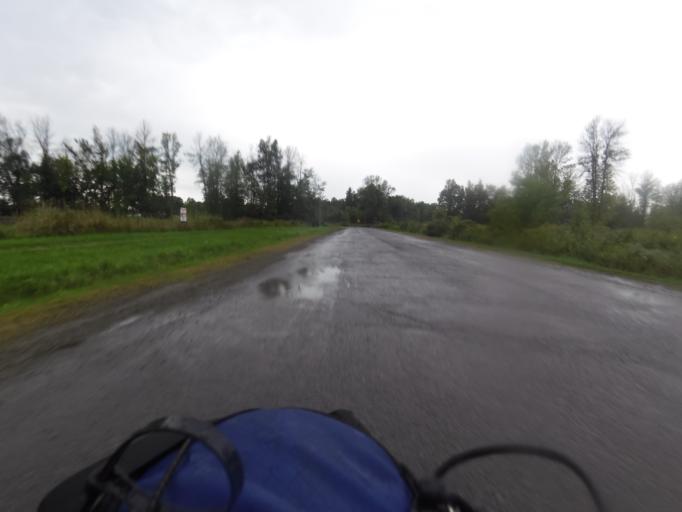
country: CA
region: Ontario
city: Ottawa
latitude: 45.2402
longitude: -75.4770
